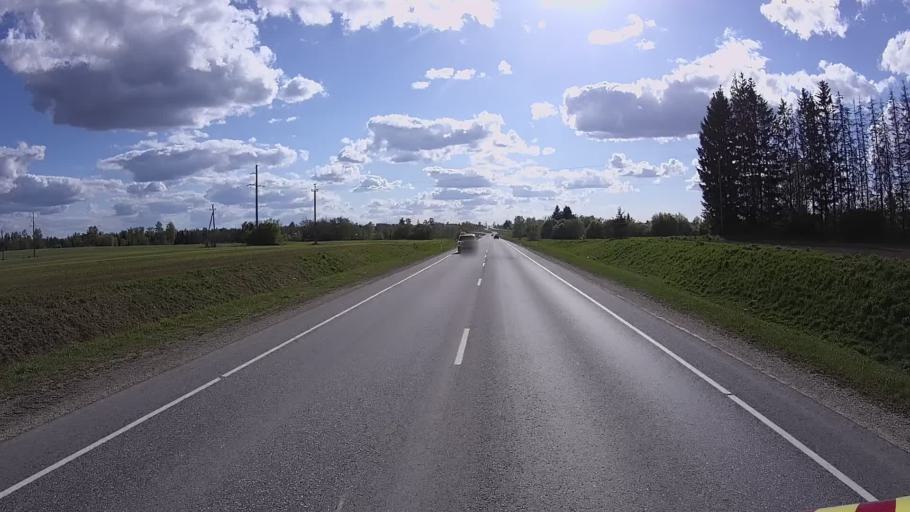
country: EE
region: Jogevamaa
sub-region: Jogeva linn
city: Jogeva
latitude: 58.7584
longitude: 26.4117
